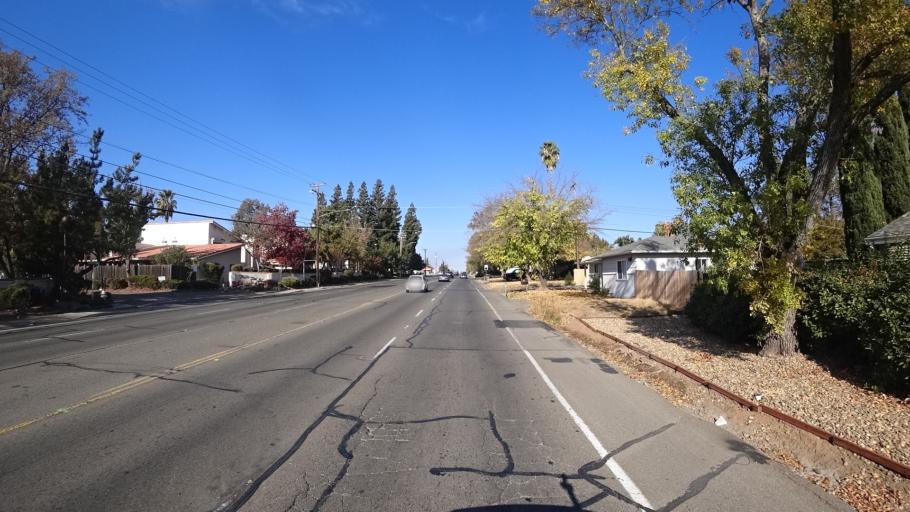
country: US
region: California
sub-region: Sacramento County
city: Fair Oaks
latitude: 38.6708
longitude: -121.2923
